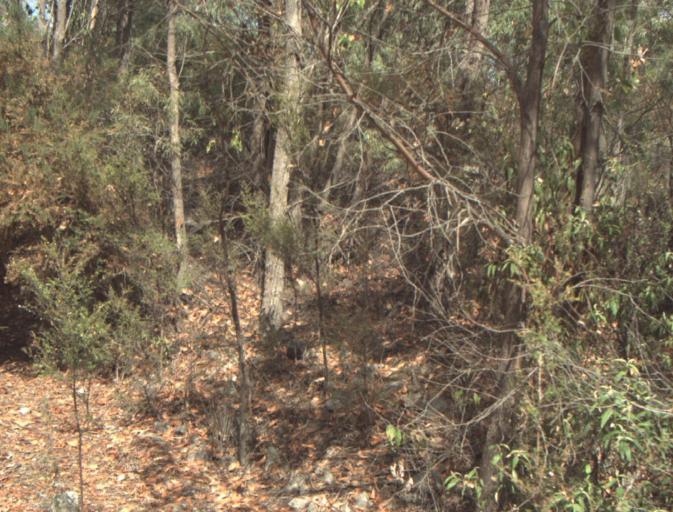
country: AU
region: Tasmania
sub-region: Launceston
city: Mayfield
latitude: -41.2030
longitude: 147.1634
